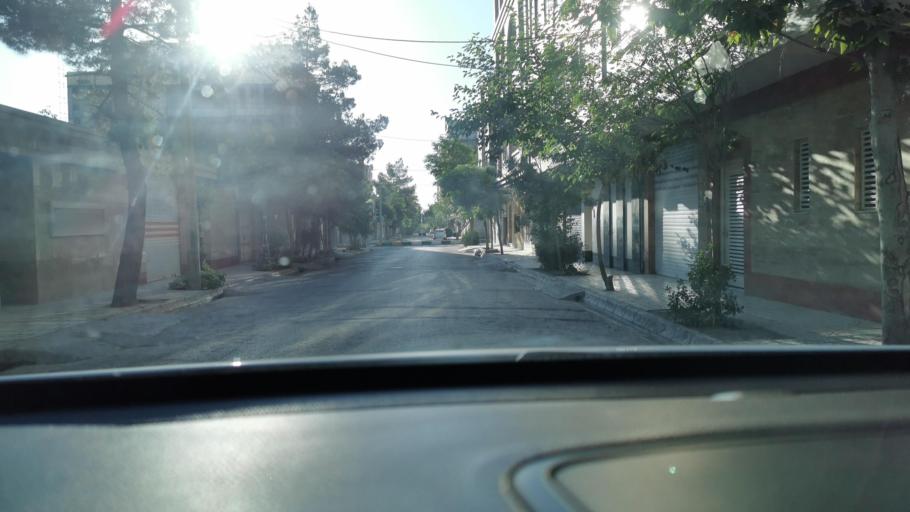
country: IR
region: Razavi Khorasan
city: Mashhad
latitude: 36.3617
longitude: 59.4896
